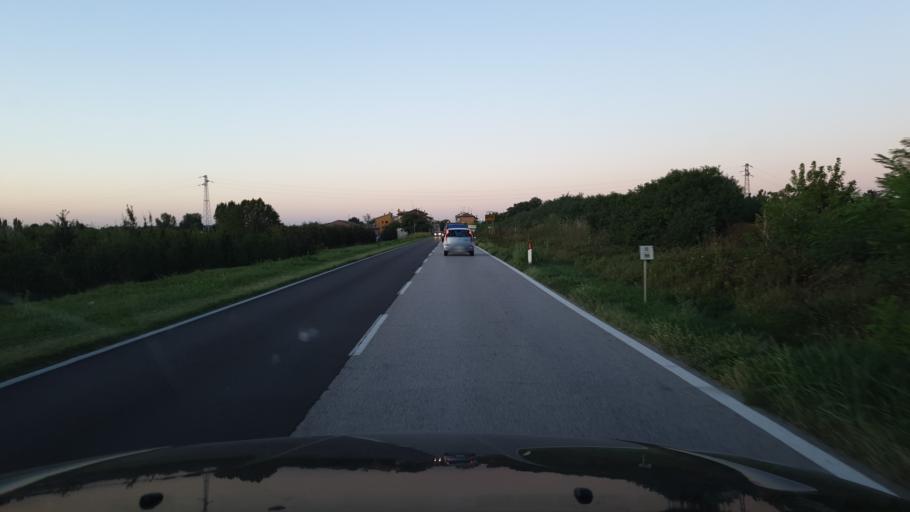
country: IT
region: Emilia-Romagna
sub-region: Provincia di Bologna
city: Ca De Fabbri
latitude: 44.6158
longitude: 11.4511
